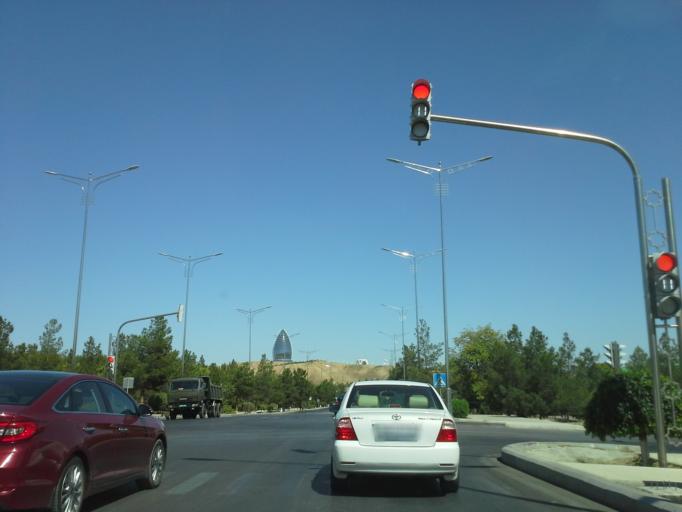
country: TM
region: Ahal
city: Ashgabat
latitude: 37.9295
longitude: 58.3102
